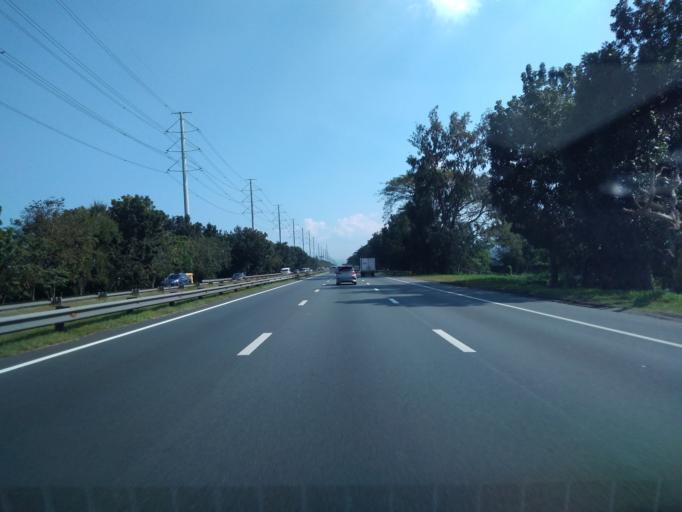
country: PH
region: Calabarzon
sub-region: Province of Laguna
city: Pulong Santa Cruz
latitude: 14.2764
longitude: 121.0929
